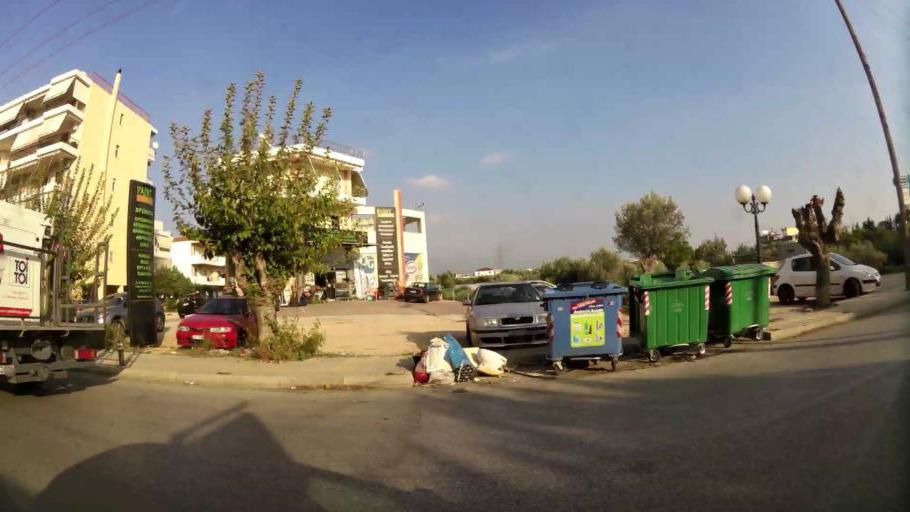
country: GR
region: Attica
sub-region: Nomarchia Anatolikis Attikis
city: Acharnes
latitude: 38.0822
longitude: 23.7453
